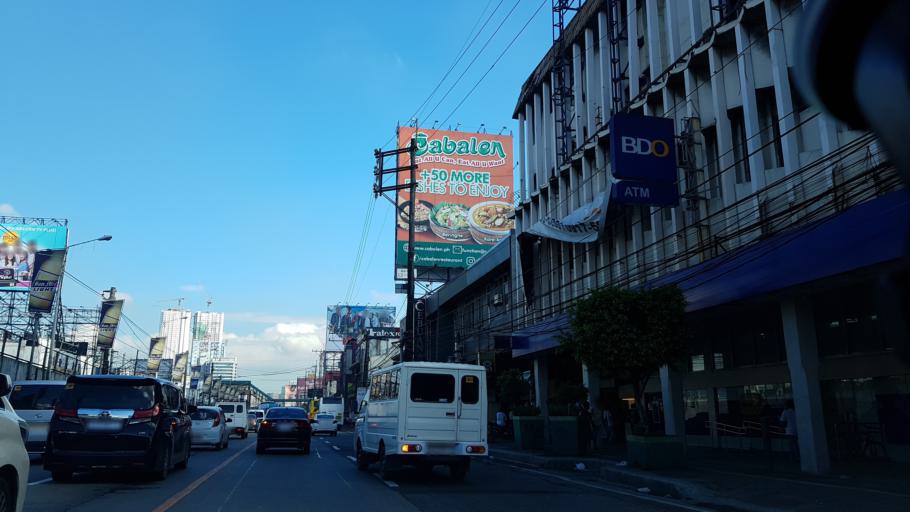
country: PH
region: Metro Manila
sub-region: Quezon City
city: Quezon City
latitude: 14.6257
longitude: 121.0483
